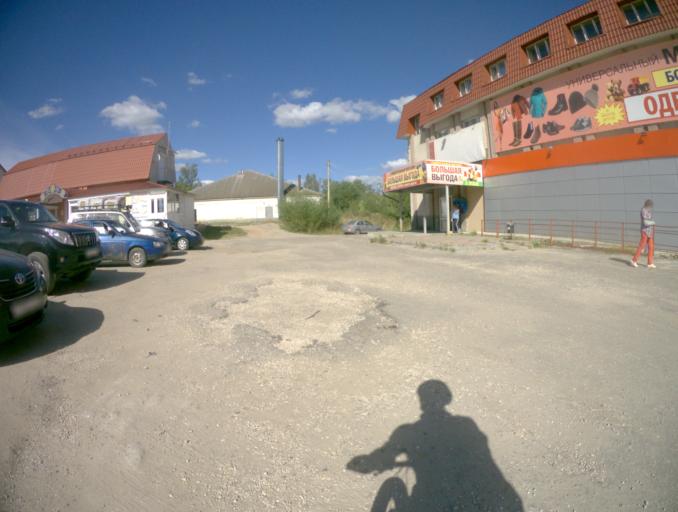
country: RU
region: Vladimir
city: Krasnaya Gorbatka
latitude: 55.8642
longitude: 41.7683
